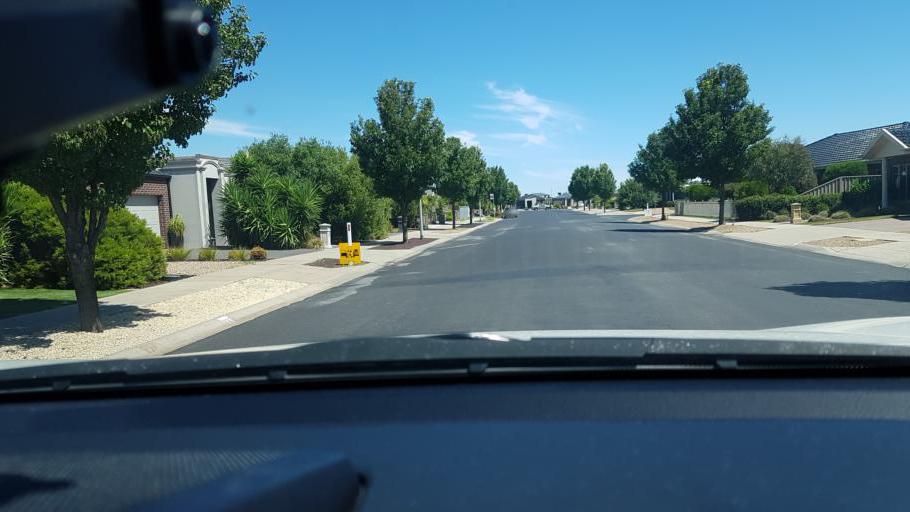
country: AU
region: Victoria
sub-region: Horsham
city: Horsham
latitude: -36.7120
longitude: 142.1812
